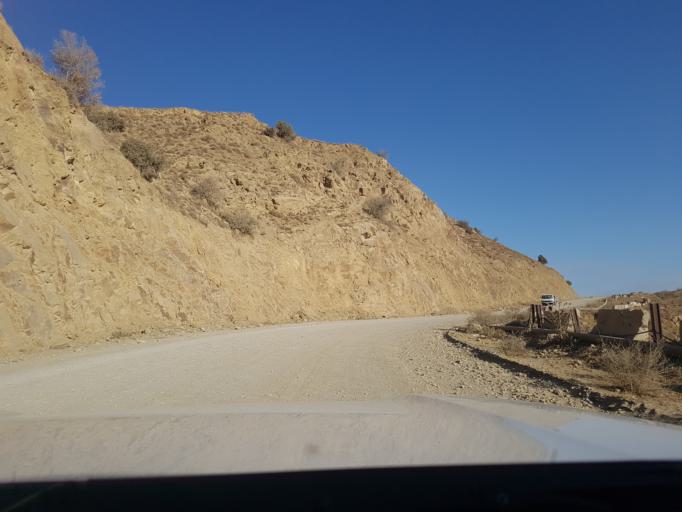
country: TM
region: Ahal
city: Baharly
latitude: 38.4425
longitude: 57.0461
